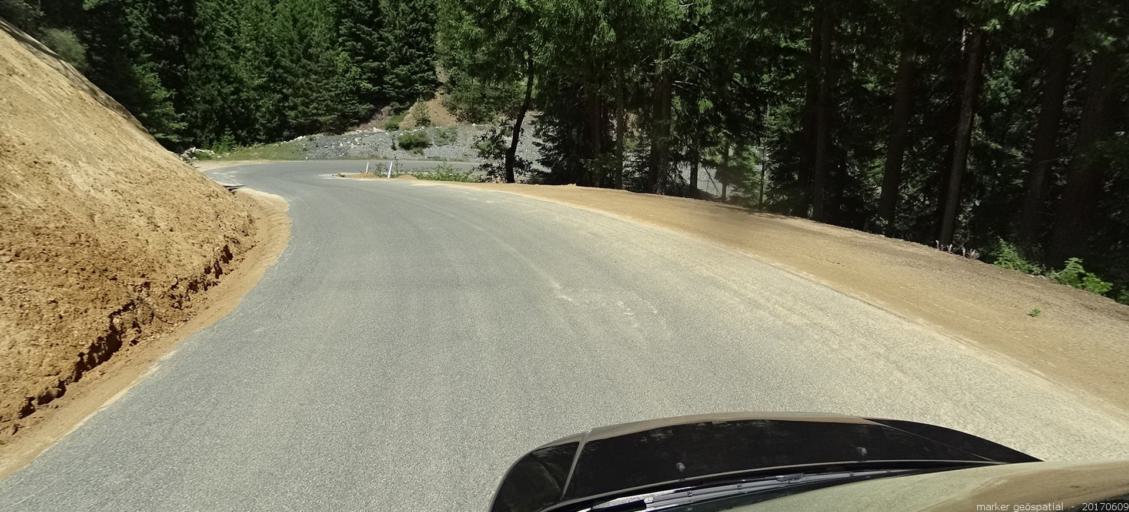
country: US
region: California
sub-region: Siskiyou County
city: Yreka
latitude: 41.4290
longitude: -122.9522
